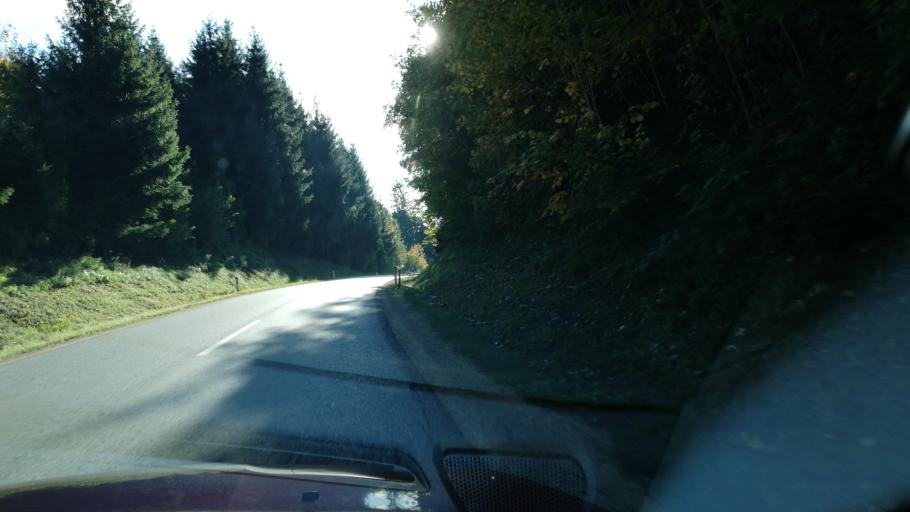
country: AT
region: Upper Austria
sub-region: Politischer Bezirk Steyr-Land
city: Ternberg
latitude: 47.9713
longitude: 14.3414
